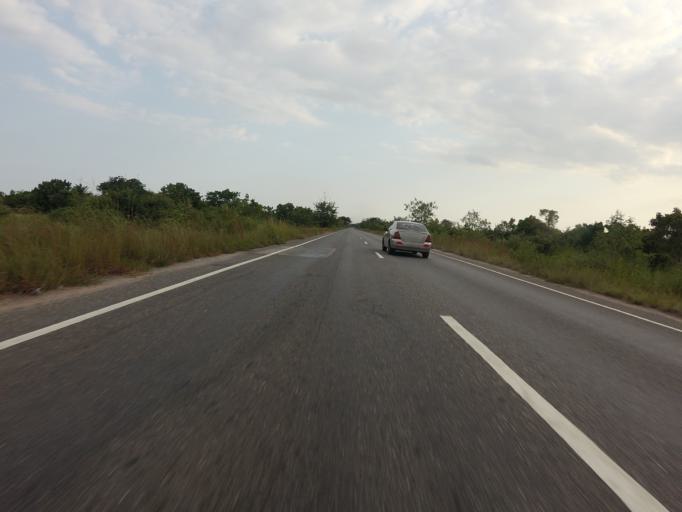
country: GH
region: Volta
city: Ho
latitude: 6.1272
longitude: 0.5226
